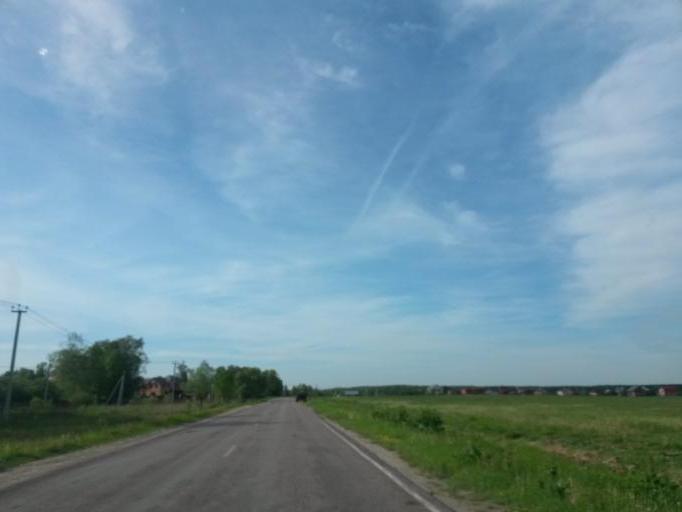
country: RU
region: Moskovskaya
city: Lyubuchany
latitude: 55.2417
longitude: 37.6416
